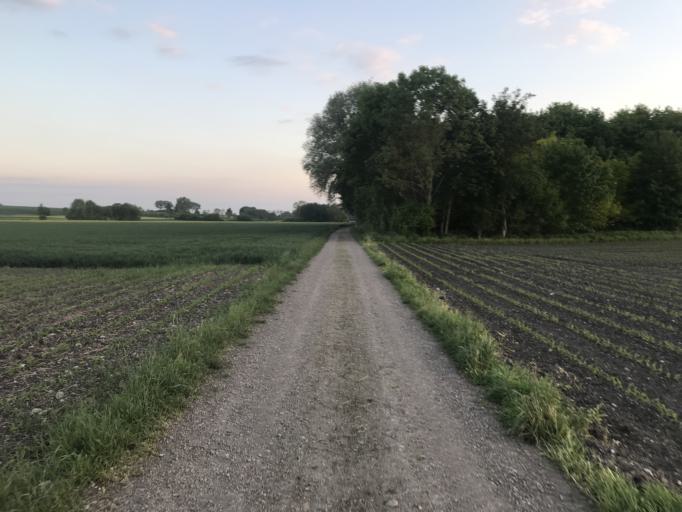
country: DE
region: Bavaria
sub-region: Swabia
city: Mering
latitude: 48.2564
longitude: 10.9646
